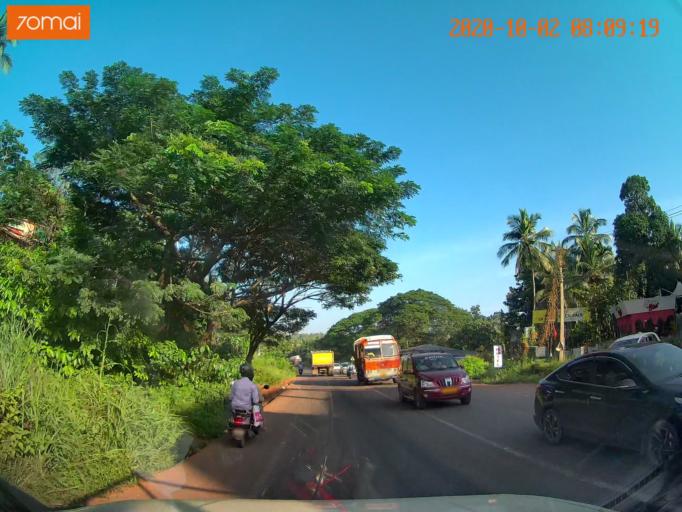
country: IN
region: Kerala
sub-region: Kozhikode
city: Kozhikode
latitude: 11.2607
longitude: 75.8202
